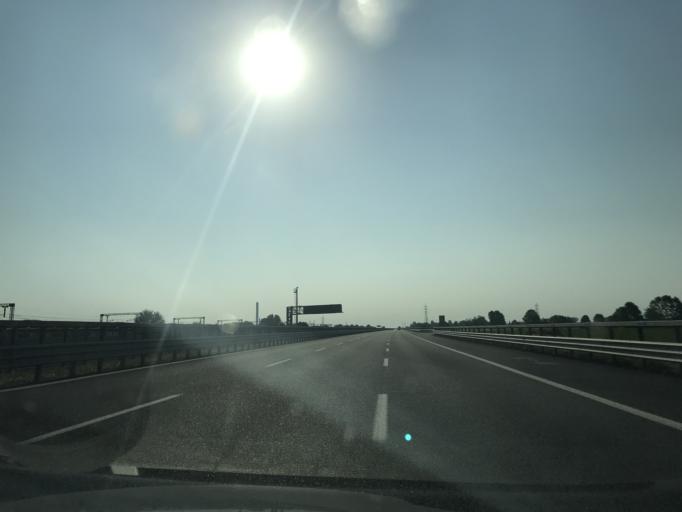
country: IT
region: Lombardy
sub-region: Citta metropolitana di Milano
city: Pozzuolo Martesana
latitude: 45.5074
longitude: 9.4648
